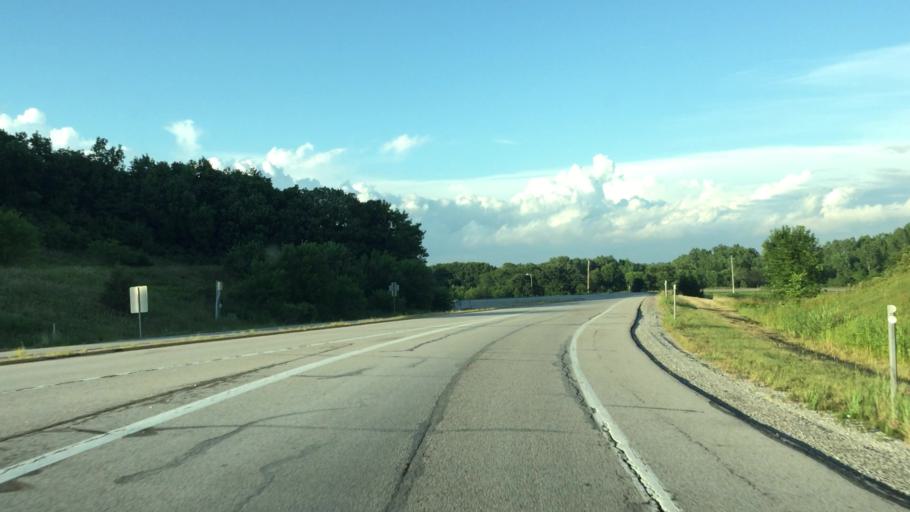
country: US
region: Iowa
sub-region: Johnson County
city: University Heights
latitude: 41.6155
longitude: -91.5481
